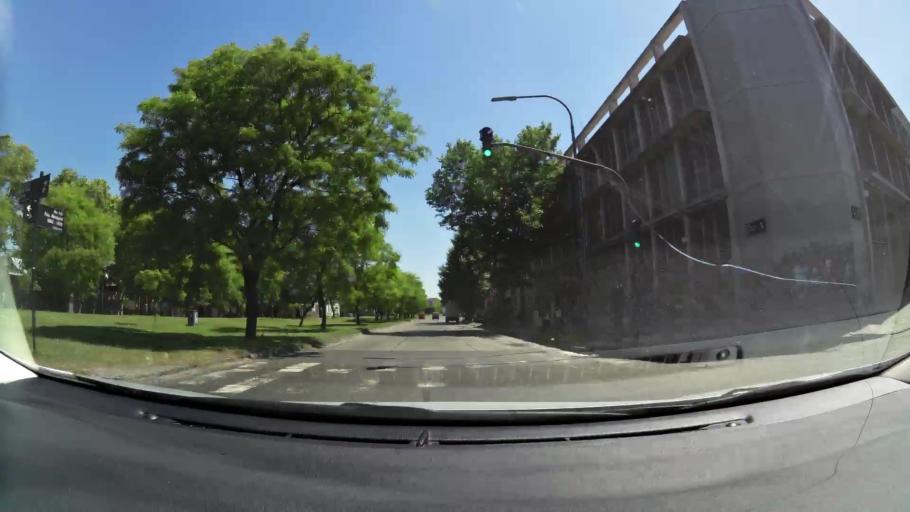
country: AR
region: Buenos Aires
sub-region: Partido de Lanus
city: Lanus
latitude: -34.6563
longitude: -58.4219
